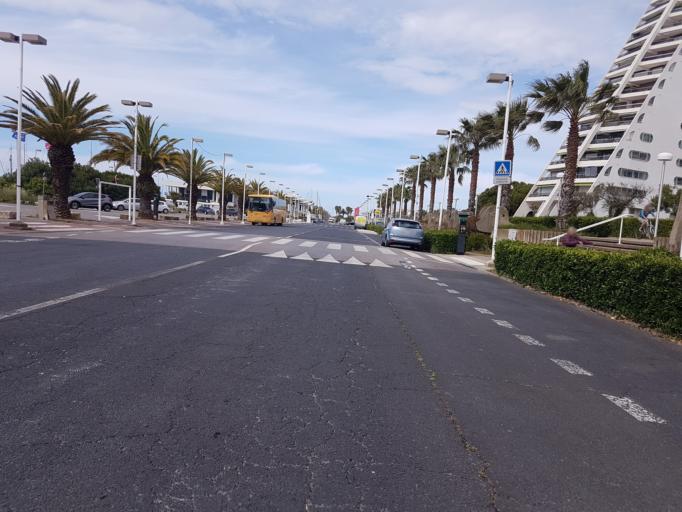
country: FR
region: Languedoc-Roussillon
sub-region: Departement de l'Herault
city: La Grande-Motte
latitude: 43.5602
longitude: 4.0803
